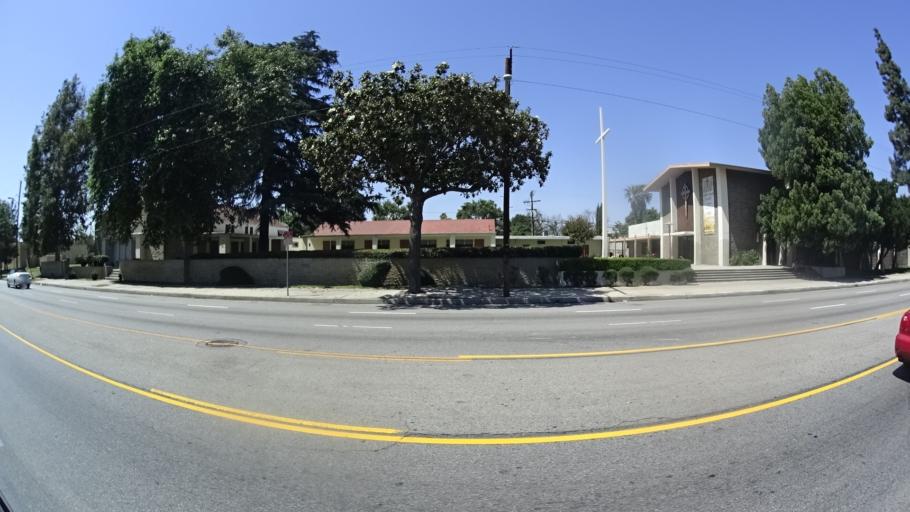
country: US
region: California
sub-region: Los Angeles County
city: Van Nuys
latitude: 34.2216
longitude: -118.4421
